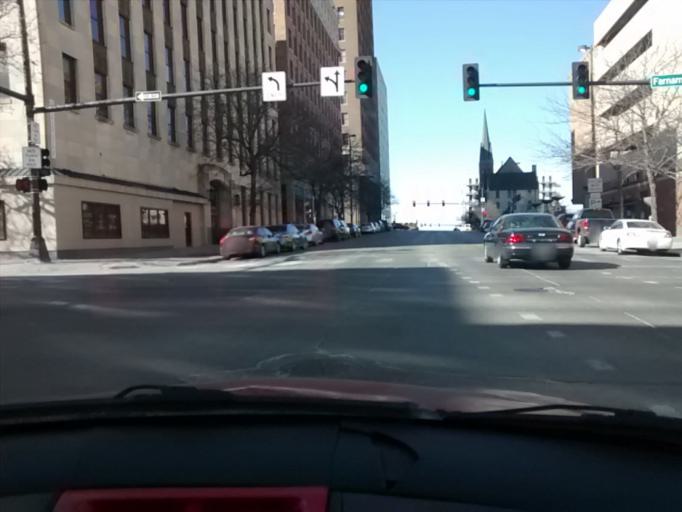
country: US
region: Nebraska
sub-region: Douglas County
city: Omaha
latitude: 41.2575
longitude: -95.9411
